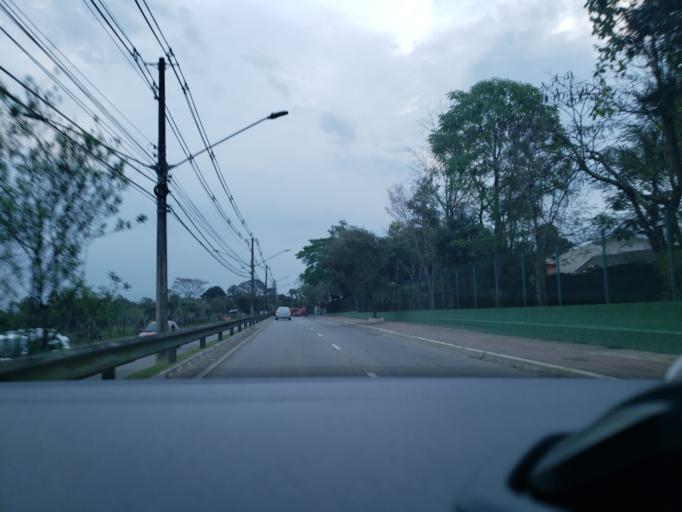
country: BR
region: Sao Paulo
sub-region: Sao Jose Dos Campos
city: Sao Jose dos Campos
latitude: -23.1931
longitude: -45.9256
